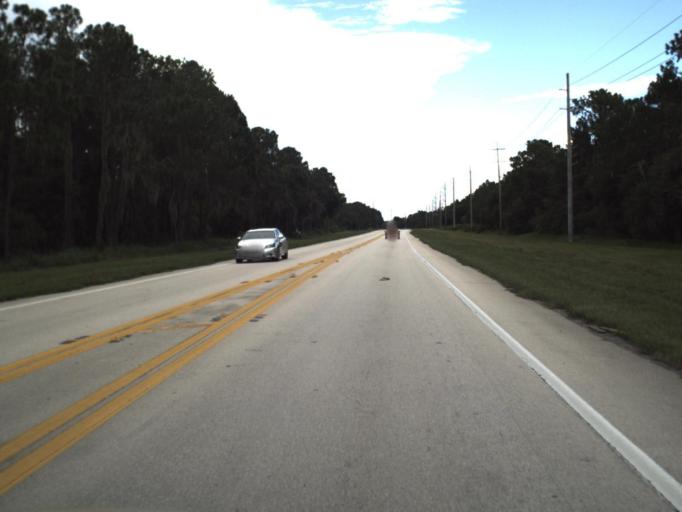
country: US
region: Florida
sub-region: Polk County
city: Mulberry
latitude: 27.7265
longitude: -82.0064
